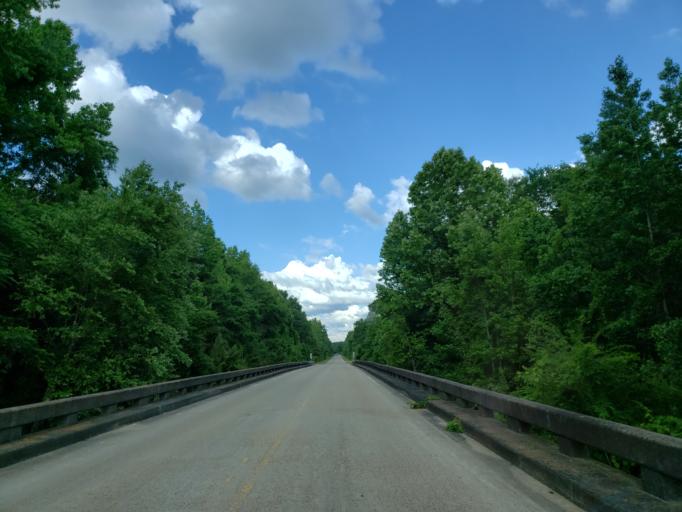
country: US
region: Mississippi
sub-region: Forrest County
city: Petal
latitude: 31.2609
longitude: -89.2259
